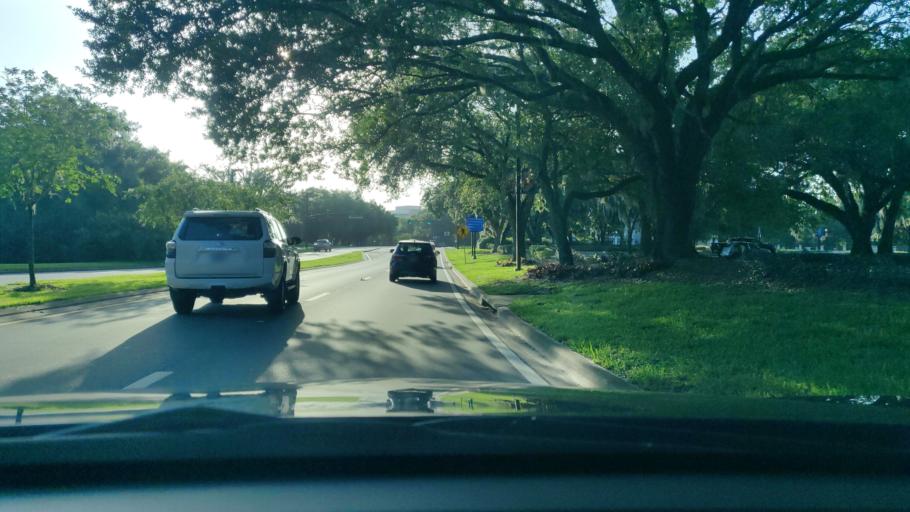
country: US
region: Florida
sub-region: Orange County
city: Orlando
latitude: 28.5706
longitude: -81.3660
